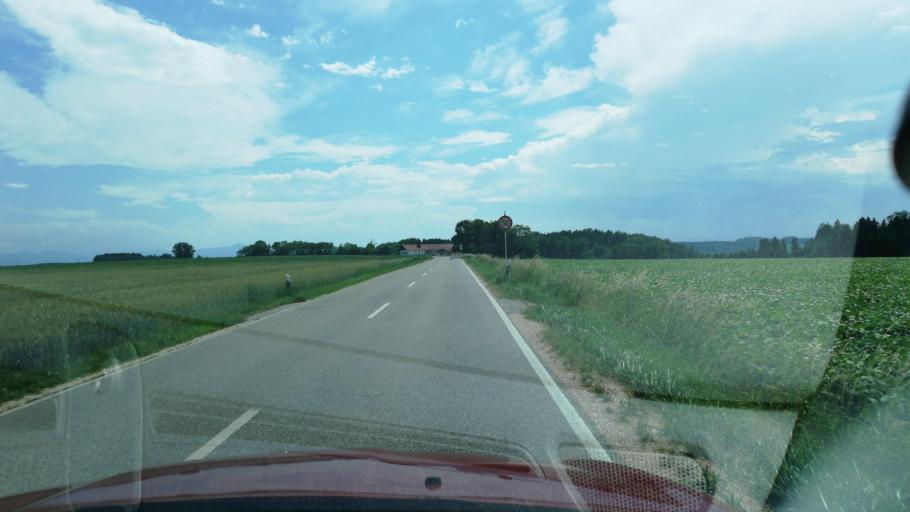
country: DE
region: Bavaria
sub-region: Upper Bavaria
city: Tacherting
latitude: 48.0714
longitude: 12.5947
